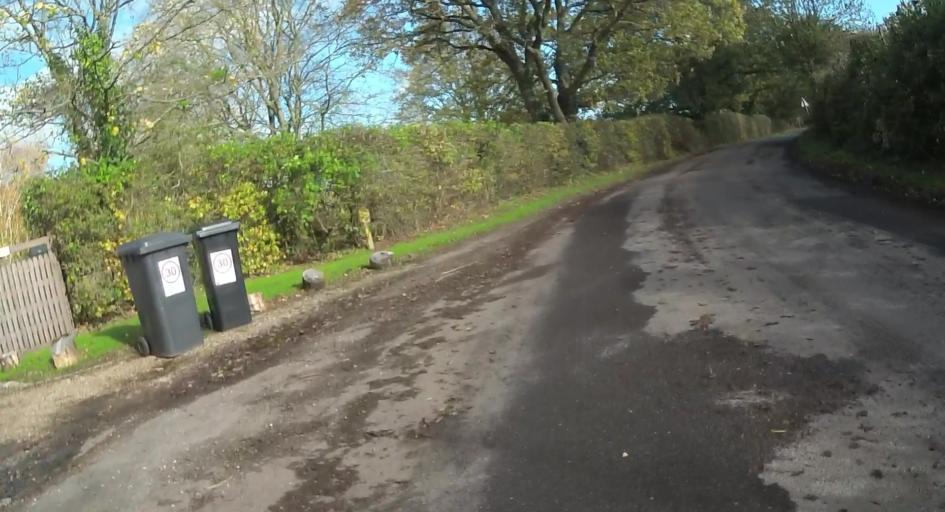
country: GB
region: England
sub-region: West Berkshire
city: Stratfield Mortimer
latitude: 51.3531
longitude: -1.0164
